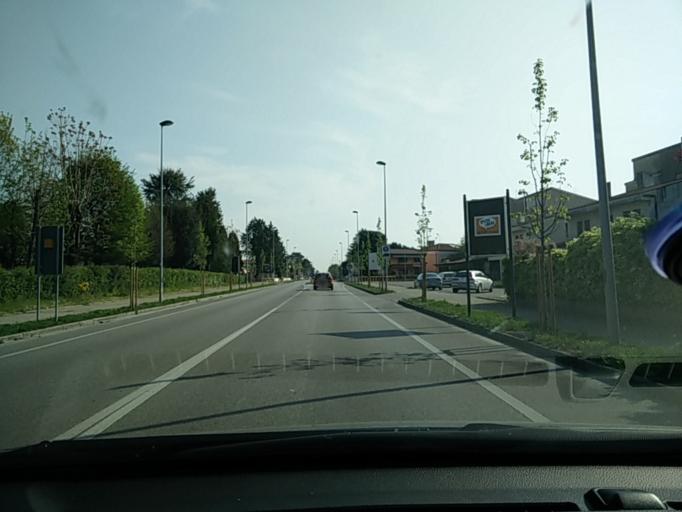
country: IT
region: Friuli Venezia Giulia
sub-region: Provincia di Pordenone
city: Prata di Pordenone
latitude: 45.8926
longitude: 12.5915
